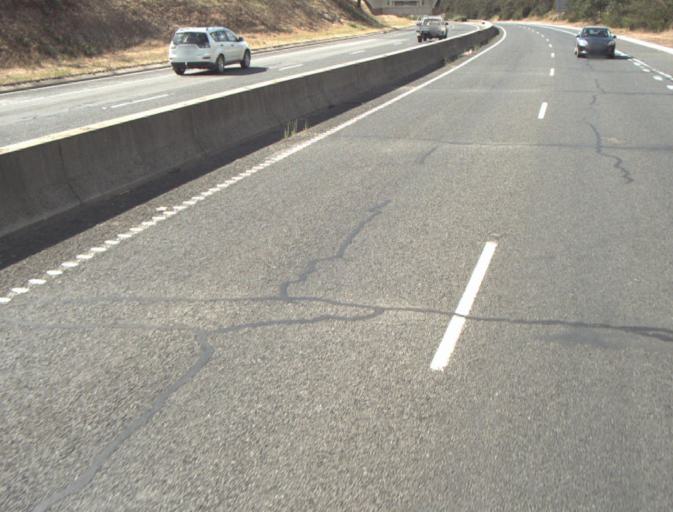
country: AU
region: Tasmania
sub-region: Launceston
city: Summerhill
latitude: -41.4756
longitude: 147.1439
